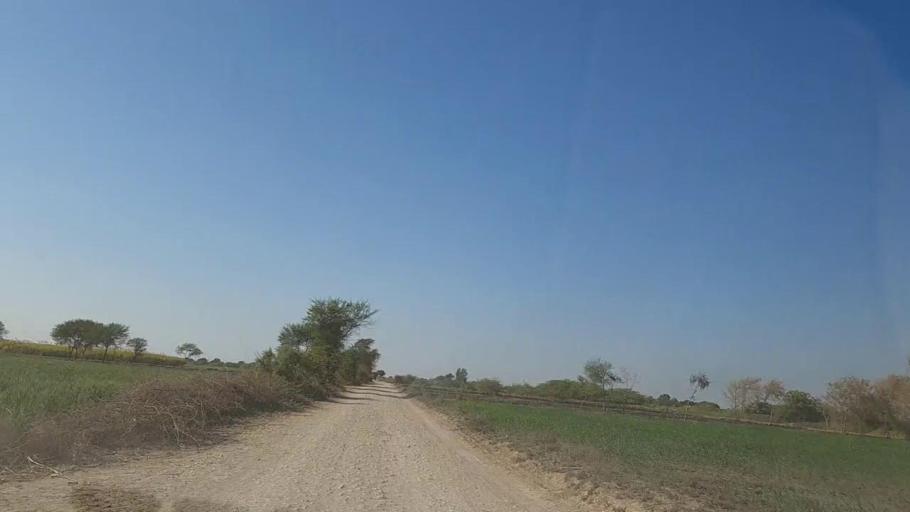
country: PK
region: Sindh
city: Digri
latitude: 25.1803
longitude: 69.0086
